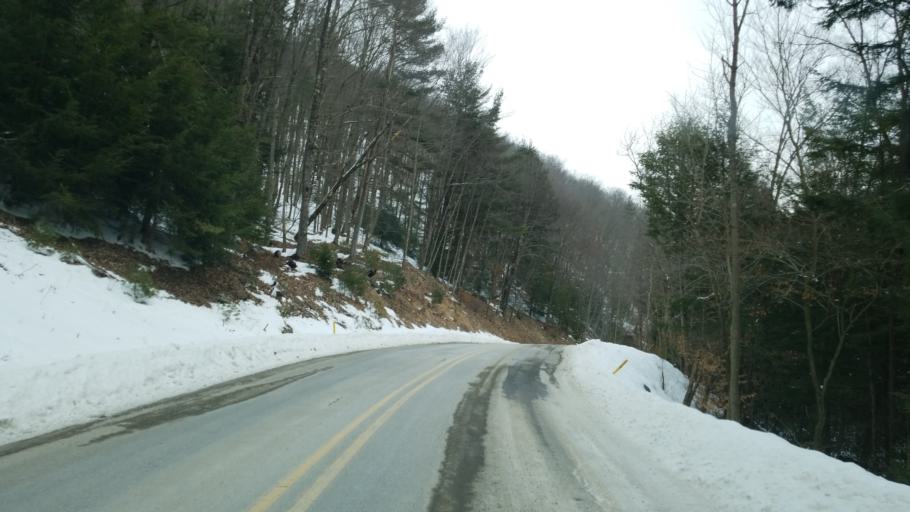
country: US
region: Pennsylvania
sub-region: Clearfield County
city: Shiloh
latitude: 41.2475
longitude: -78.1602
